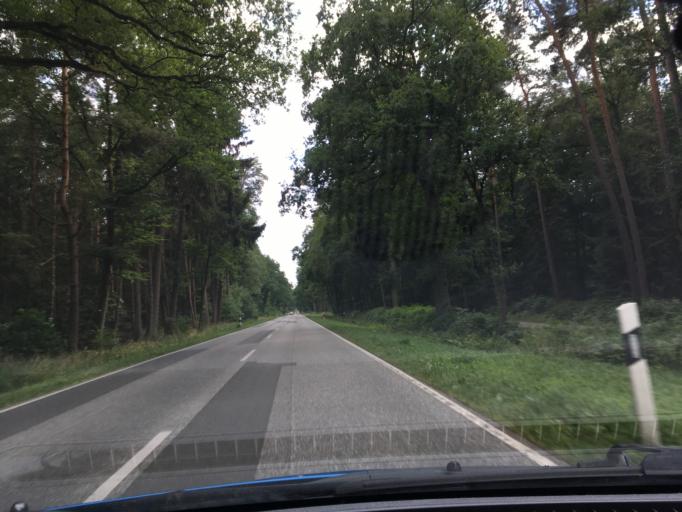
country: DE
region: Mecklenburg-Vorpommern
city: Lubtheen
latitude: 53.3484
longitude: 11.0846
